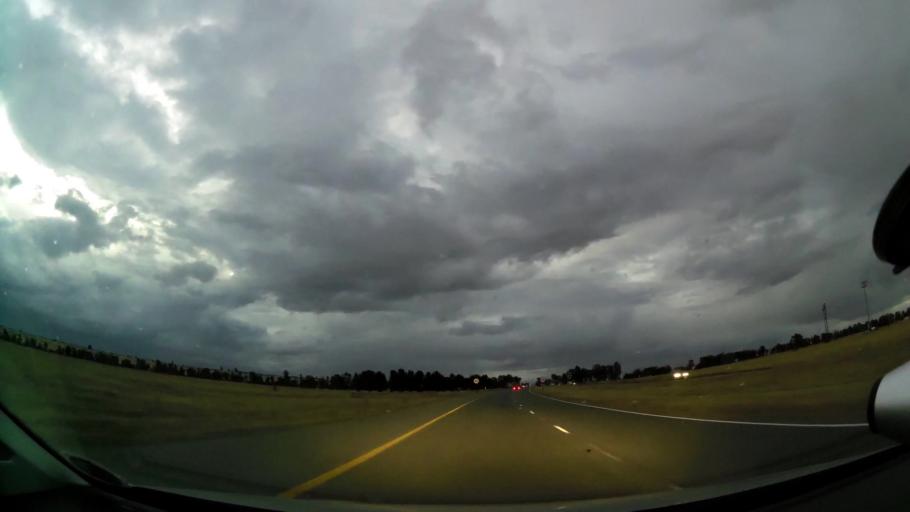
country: ZA
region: Orange Free State
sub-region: Lejweleputswa District Municipality
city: Welkom
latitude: -27.9411
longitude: 26.7896
